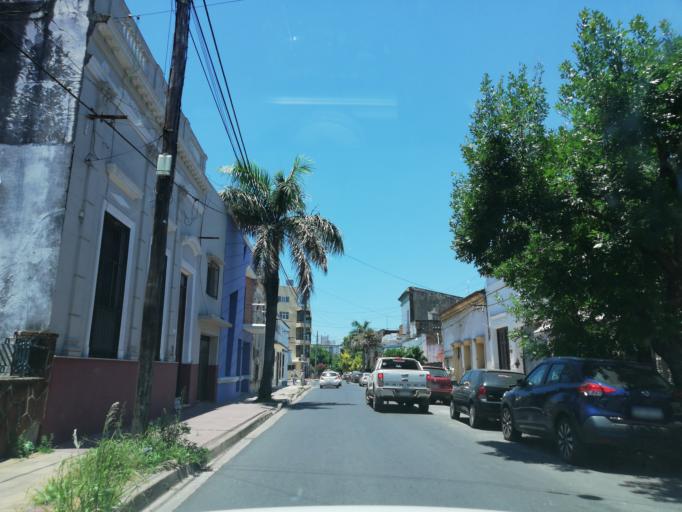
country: AR
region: Corrientes
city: Corrientes
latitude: -27.4625
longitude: -58.8318
